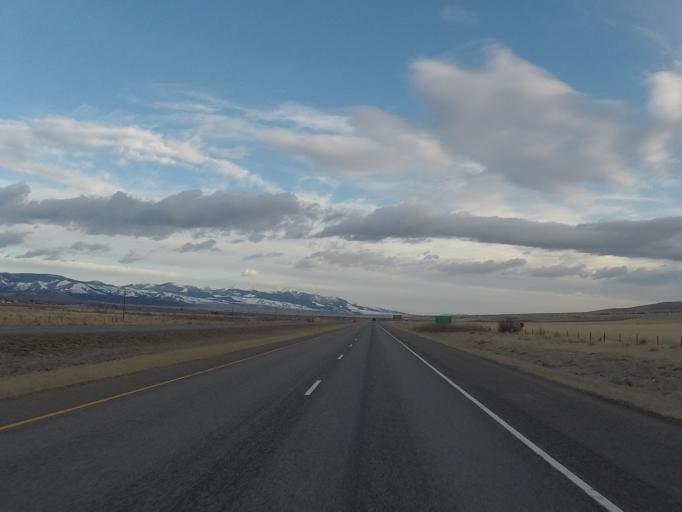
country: US
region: Montana
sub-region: Deer Lodge County
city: Warm Springs
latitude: 46.0802
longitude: -112.7874
